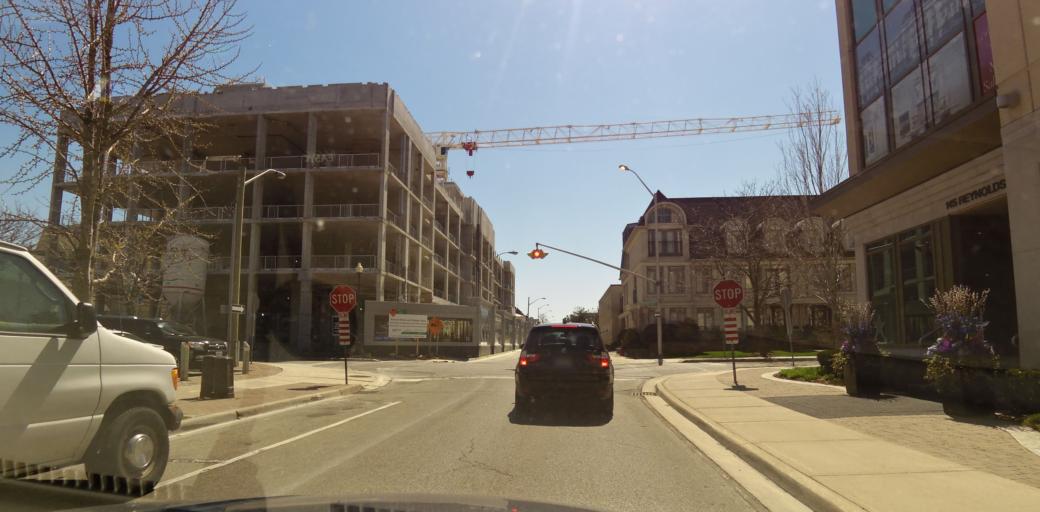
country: CA
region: Ontario
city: Oakville
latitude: 43.4493
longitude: -79.6670
